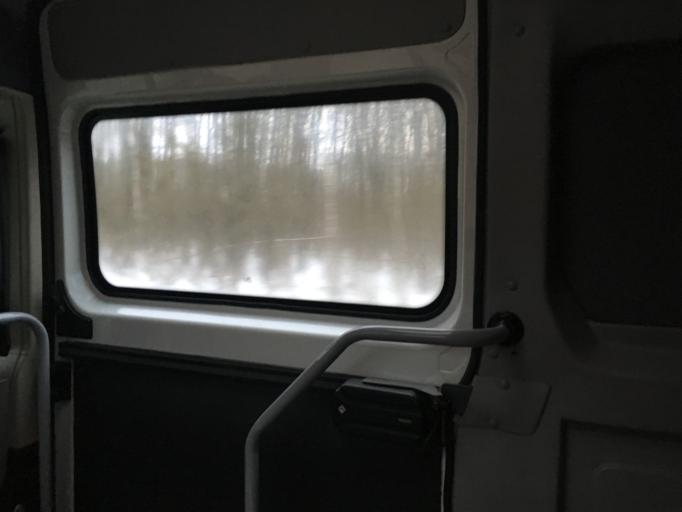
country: RU
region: Tula
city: Krapivna
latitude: 54.1294
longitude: 37.2519
